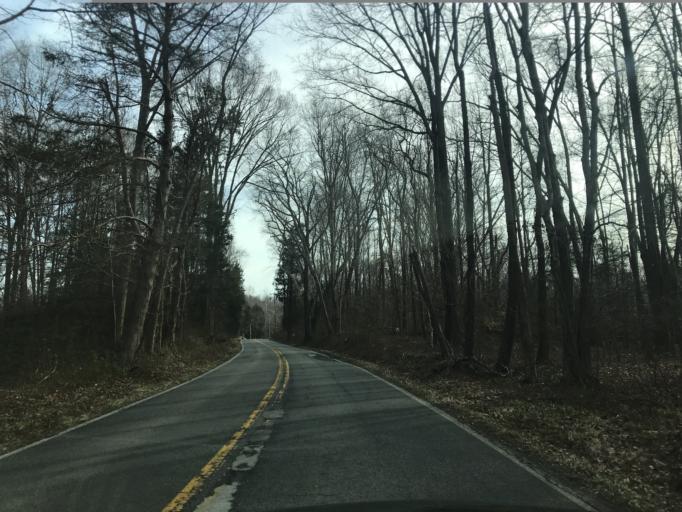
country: US
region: Virginia
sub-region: King George County
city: King George
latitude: 38.4193
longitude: -77.1962
